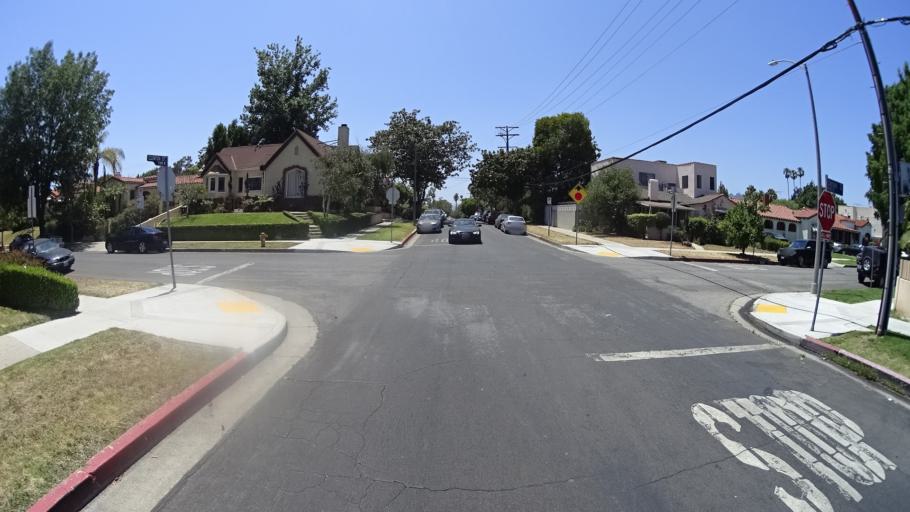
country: US
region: California
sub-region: Los Angeles County
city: West Hollywood
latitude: 34.0819
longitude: -118.3450
